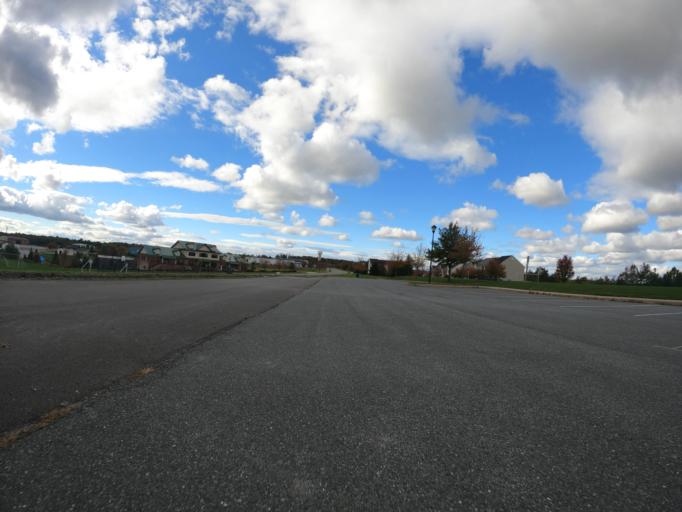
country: US
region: Maryland
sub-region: Carroll County
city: Mount Airy
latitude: 39.3658
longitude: -77.1302
